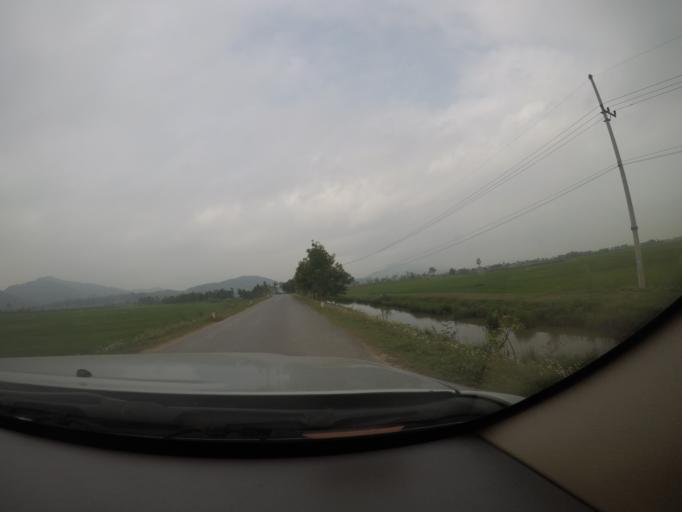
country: VN
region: Quang Binh
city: Ba Don
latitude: 17.6983
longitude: 106.4359
